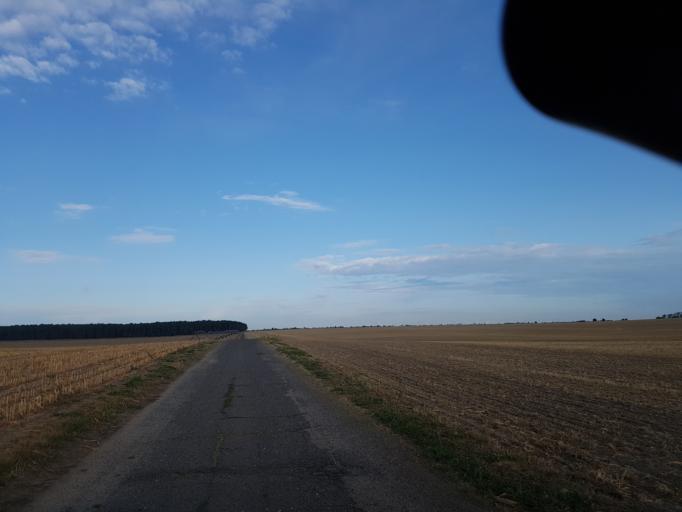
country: DE
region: Brandenburg
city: Niedergorsdorf
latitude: 51.9322
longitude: 13.0219
